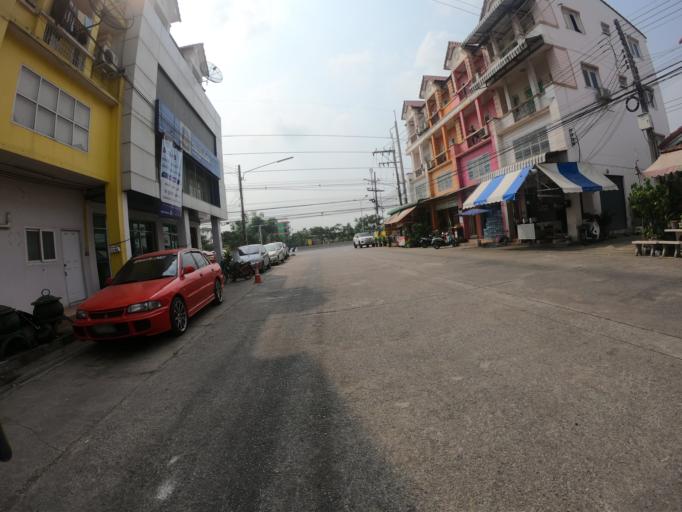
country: TH
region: Pathum Thani
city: Nong Suea
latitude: 14.0654
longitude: 100.8587
